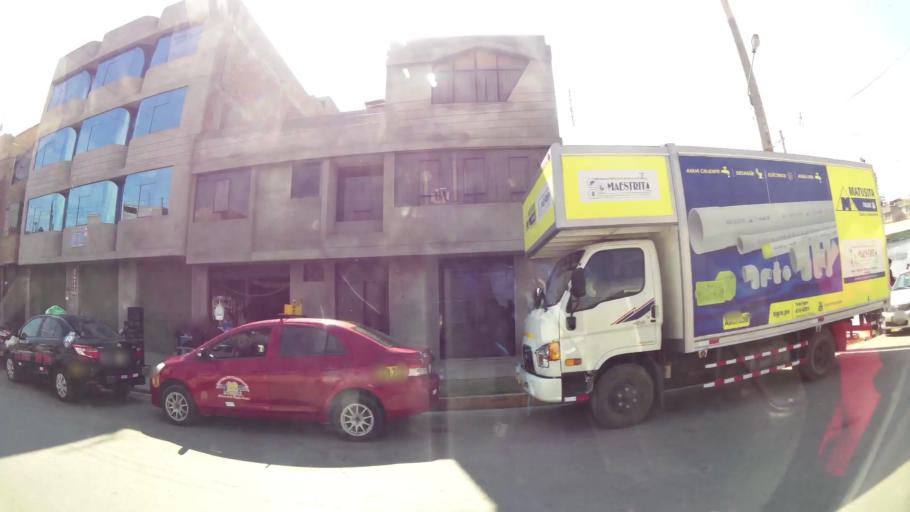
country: PE
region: Junin
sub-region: Provincia de Huancayo
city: El Tambo
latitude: -12.0756
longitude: -75.2236
